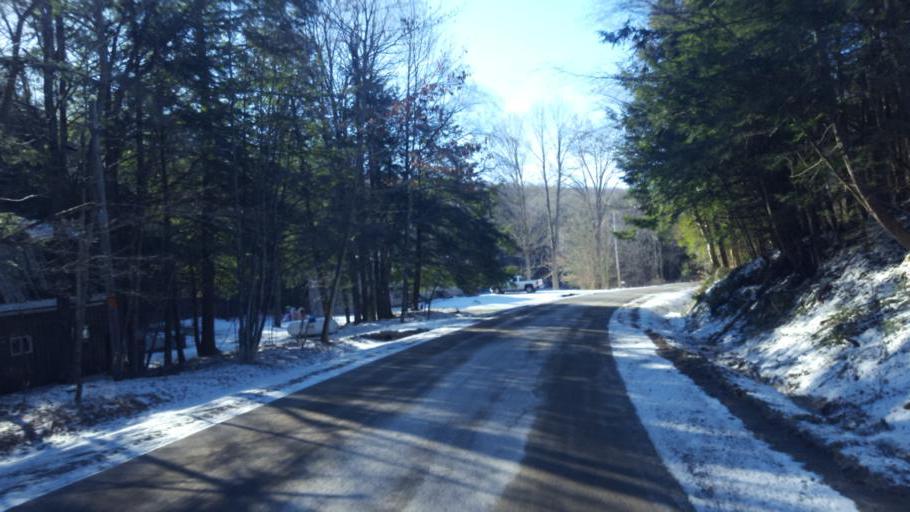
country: US
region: New York
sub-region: Allegany County
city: Wellsville
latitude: 42.1470
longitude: -77.9065
